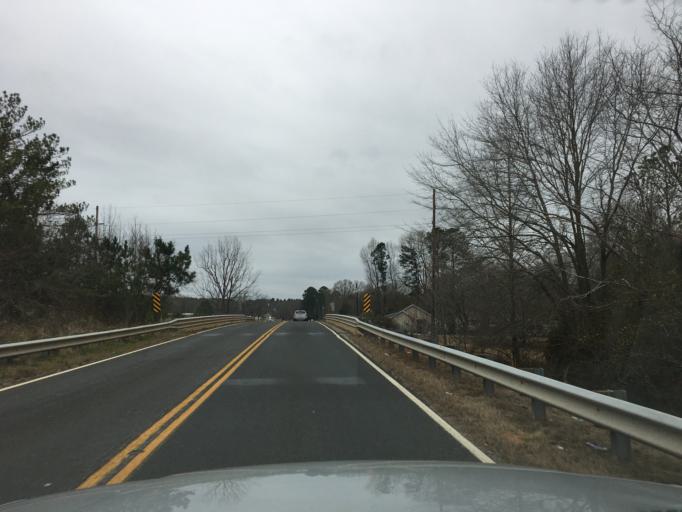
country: US
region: South Carolina
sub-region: Greenwood County
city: Greenwood
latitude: 34.1475
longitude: -82.1437
